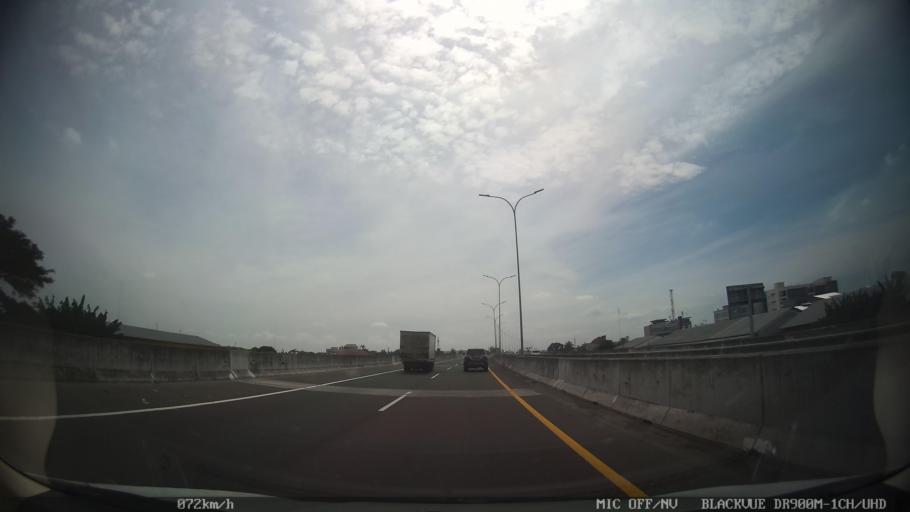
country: ID
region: North Sumatra
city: Medan
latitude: 3.6494
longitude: 98.6585
